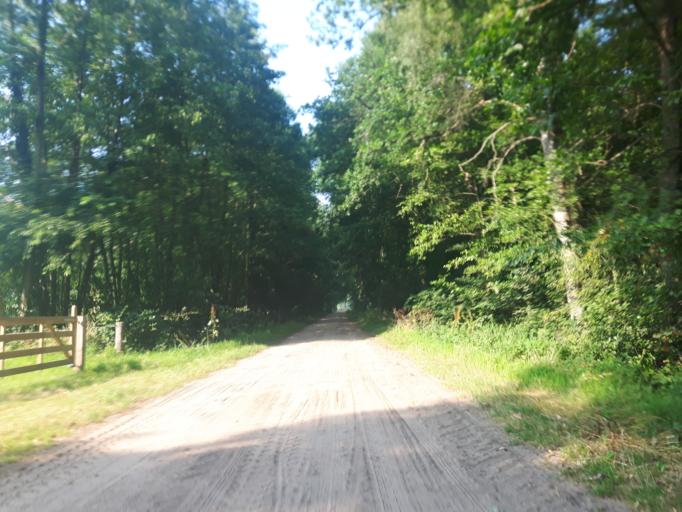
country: NL
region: Overijssel
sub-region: Gemeente Haaksbergen
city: Haaksbergen
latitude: 52.1912
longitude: 6.8055
